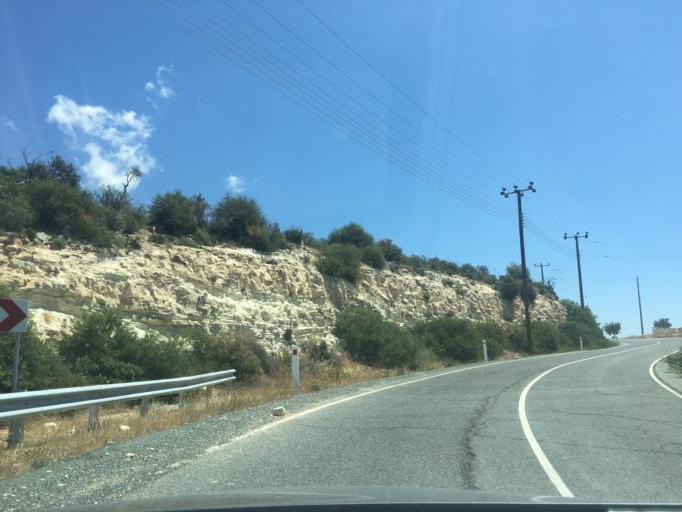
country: CY
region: Limassol
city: Mouttagiaka
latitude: 34.7527
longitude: 33.0568
